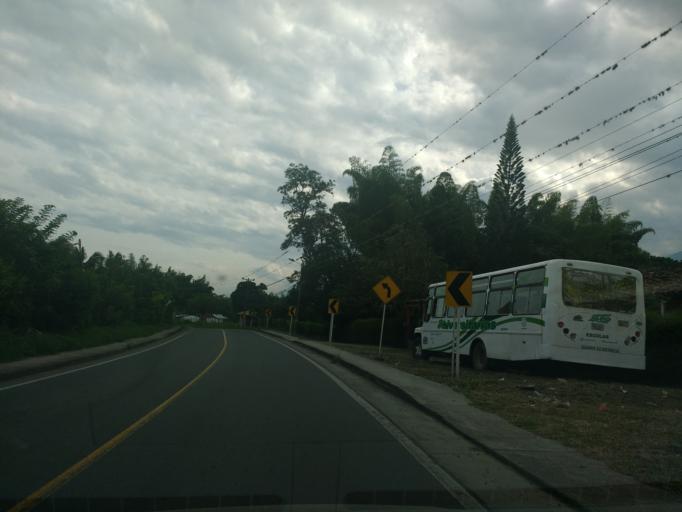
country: CO
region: Cauca
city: Miranda
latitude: 3.2767
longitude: -76.2214
